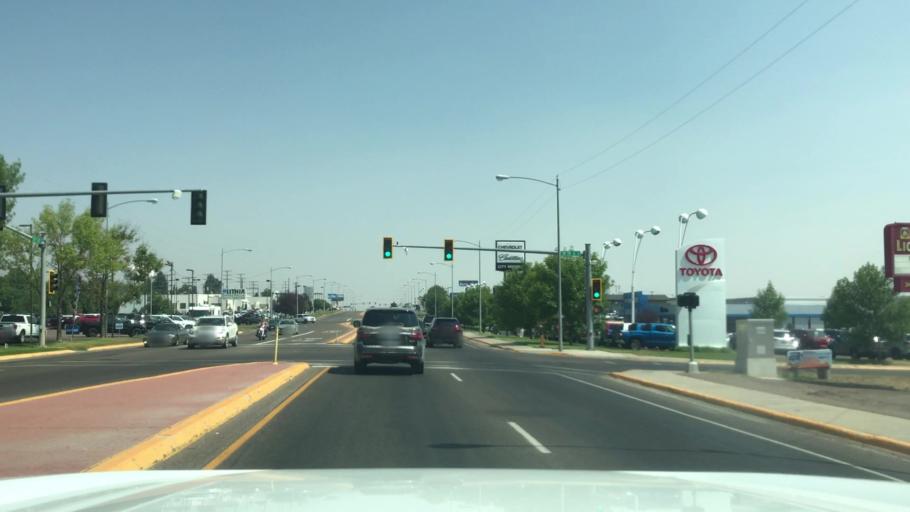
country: US
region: Montana
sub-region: Cascade County
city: Malmstrom Air Force Base
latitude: 47.4939
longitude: -111.2405
